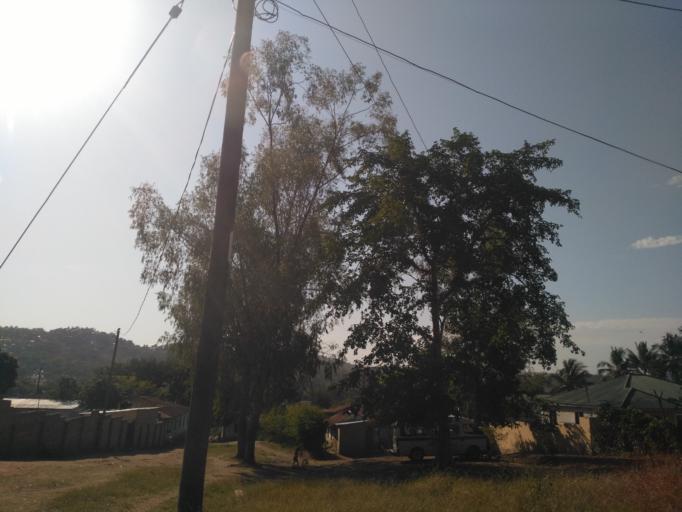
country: TZ
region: Mwanza
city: Mwanza
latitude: -2.5008
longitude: 32.8953
